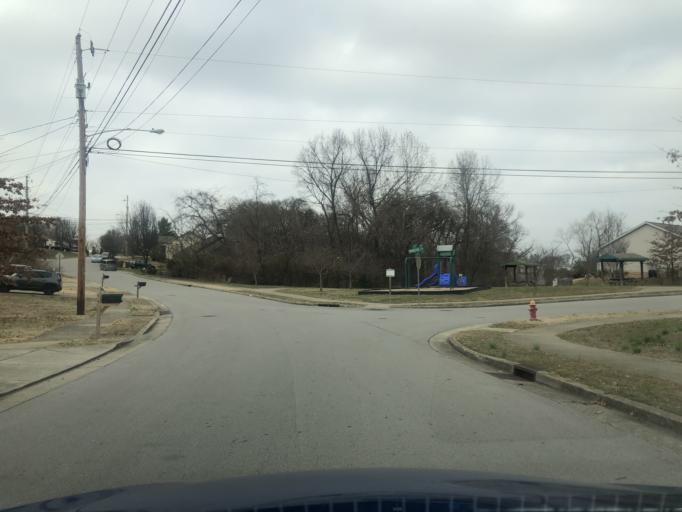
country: US
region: Tennessee
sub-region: Davidson County
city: Oak Hill
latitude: 36.0907
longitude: -86.7061
